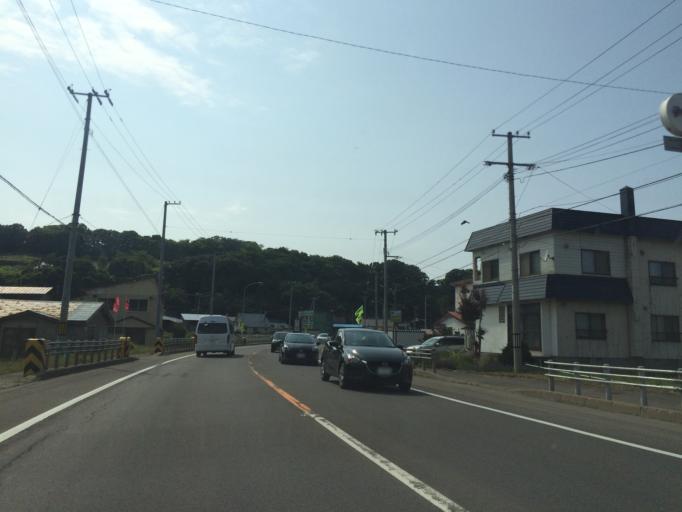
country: JP
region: Hokkaido
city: Yoichi
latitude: 43.1965
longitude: 140.8498
